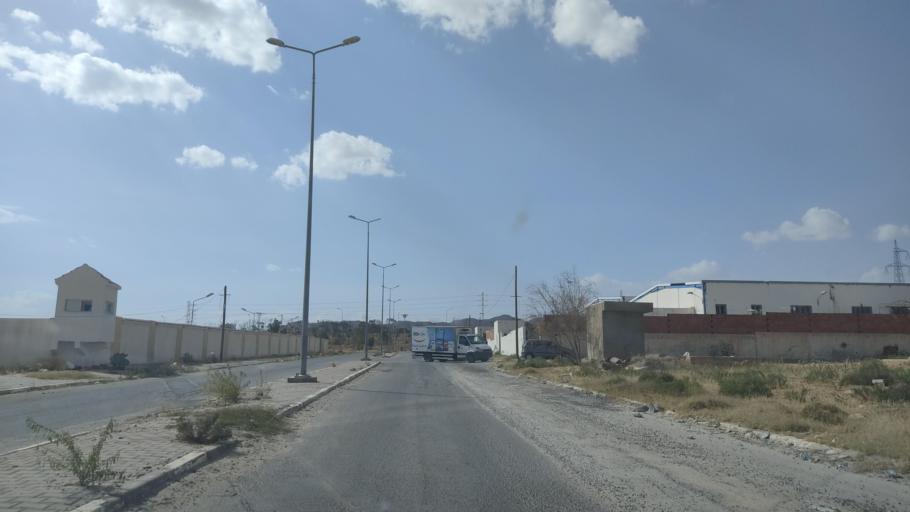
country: TN
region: Sidi Bu Zayd
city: Sidi Bouzid
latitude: 35.1082
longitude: 9.5432
